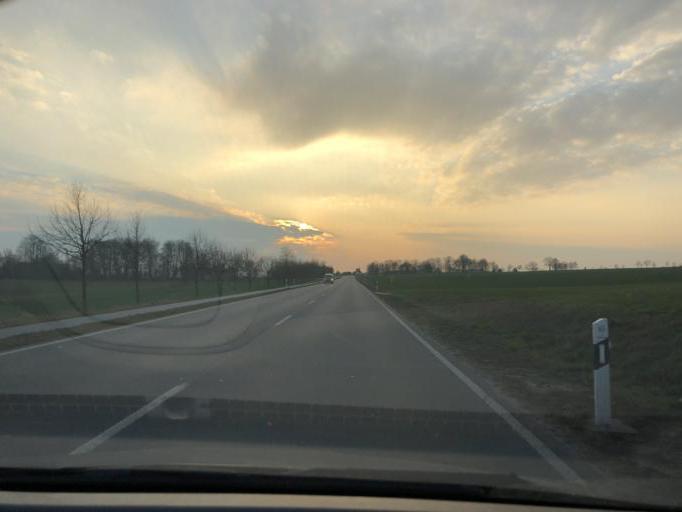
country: DE
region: Saxony
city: Obergurig
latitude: 51.1794
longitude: 14.3745
